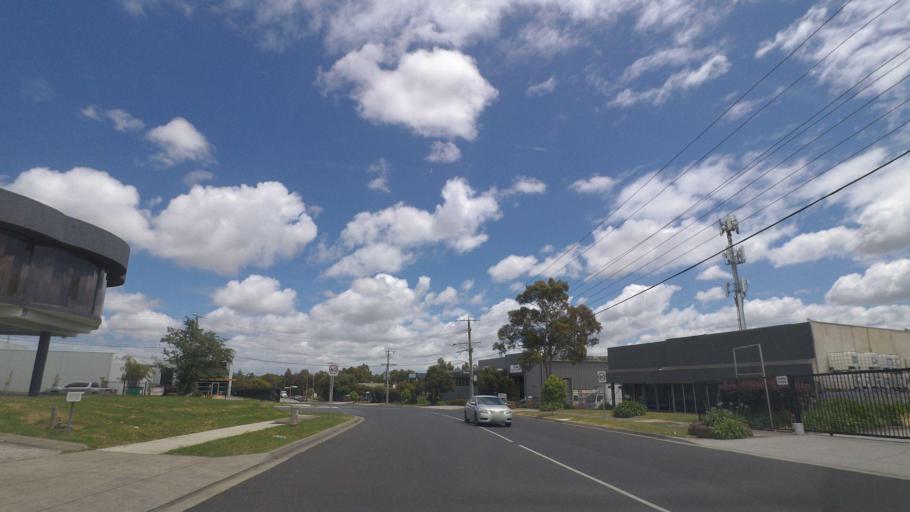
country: AU
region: Victoria
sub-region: Knox
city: Scoresby
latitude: -37.9054
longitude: 145.2461
